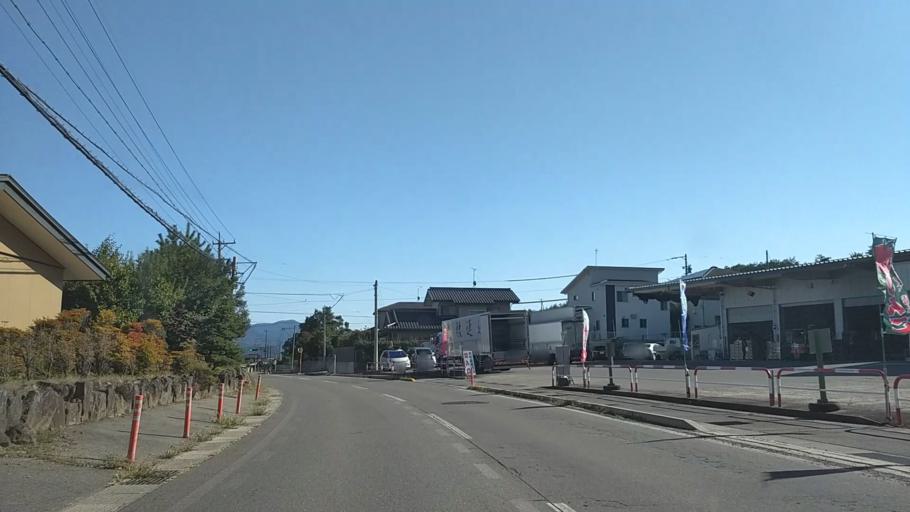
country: JP
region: Nagano
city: Nagano-shi
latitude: 36.5985
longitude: 138.1312
